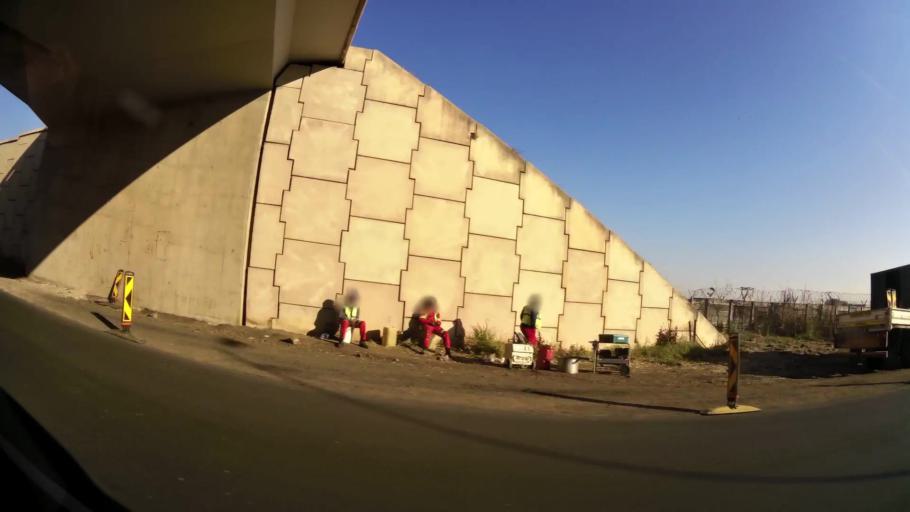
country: ZA
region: Gauteng
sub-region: City of Tshwane Metropolitan Municipality
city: Pretoria
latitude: -25.6377
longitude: 28.1989
